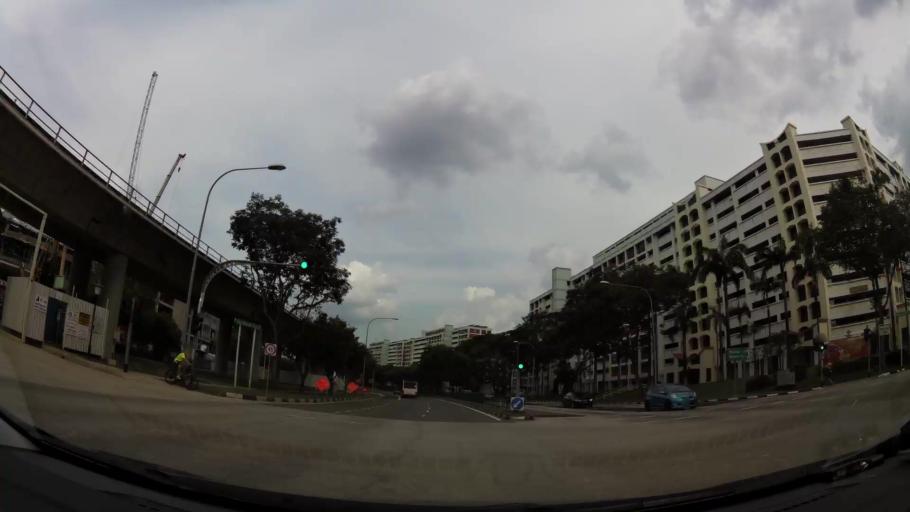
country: MY
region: Johor
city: Johor Bahru
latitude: 1.4325
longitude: 103.7794
